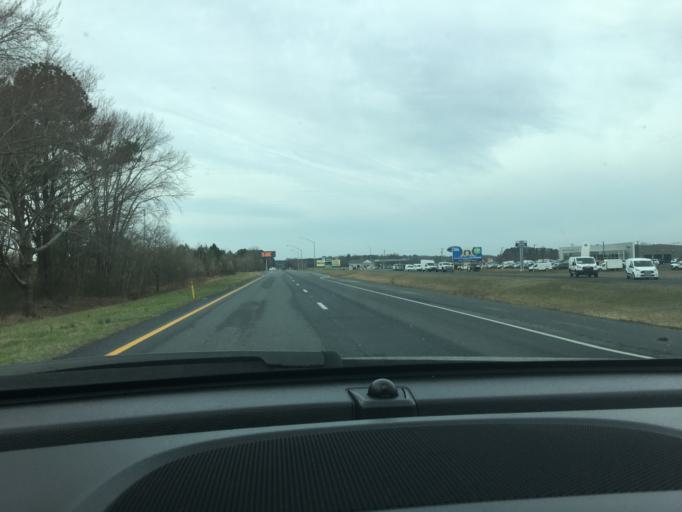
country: US
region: Maryland
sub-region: Wicomico County
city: Pittsville
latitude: 38.3850
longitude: -75.4021
